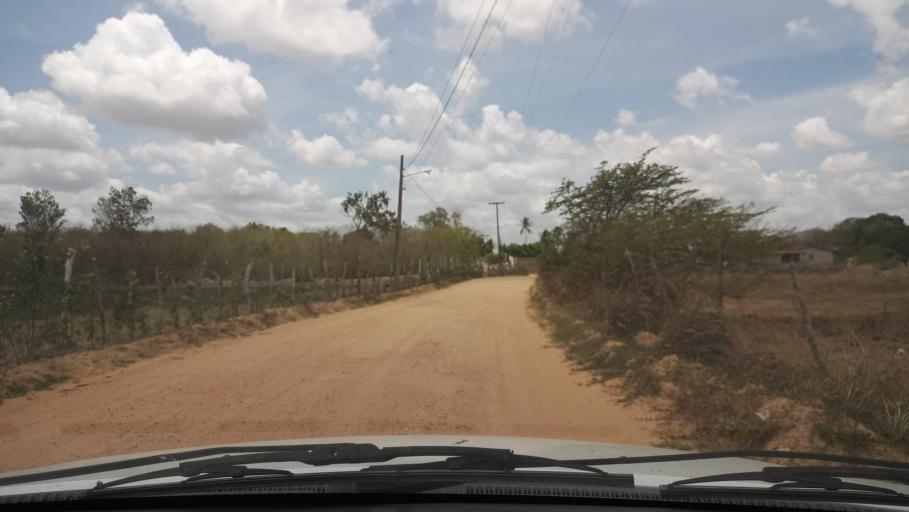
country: BR
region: Rio Grande do Norte
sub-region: Brejinho
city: Brejinho
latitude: -6.2928
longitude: -35.3441
